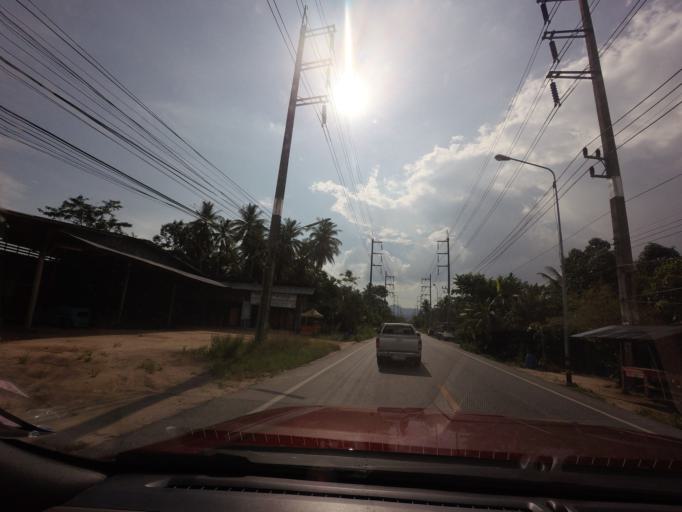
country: TH
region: Yala
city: Yala
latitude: 6.5706
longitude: 101.2044
